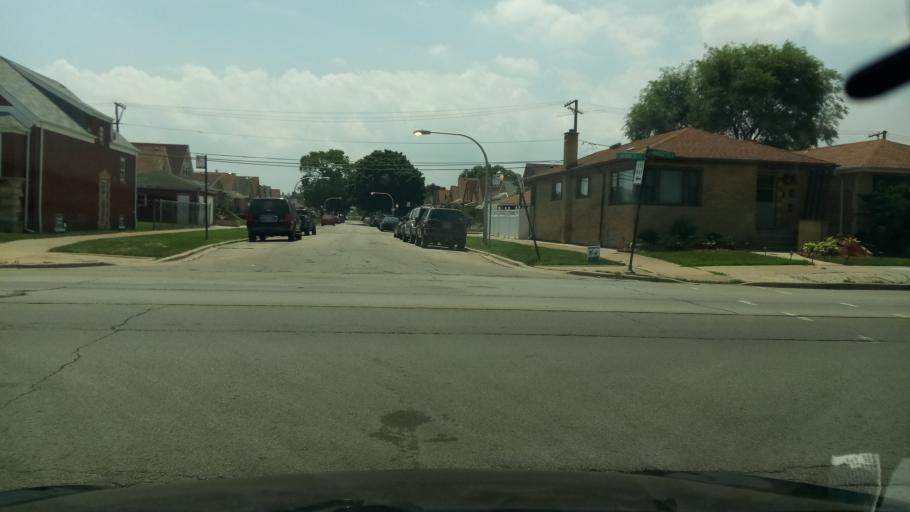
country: US
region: Illinois
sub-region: Cook County
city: Hometown
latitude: 41.7719
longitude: -87.7335
